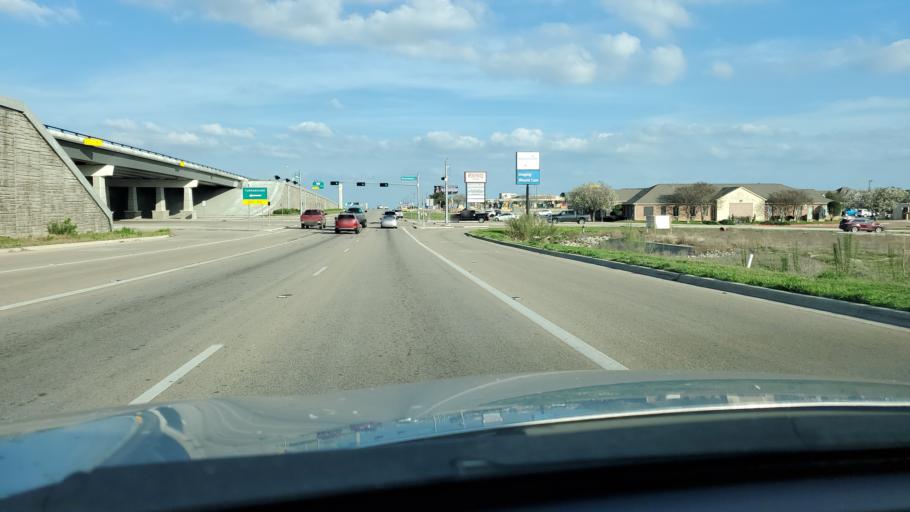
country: US
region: Texas
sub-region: Bell County
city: Harker Heights
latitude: 31.0760
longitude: -97.6894
